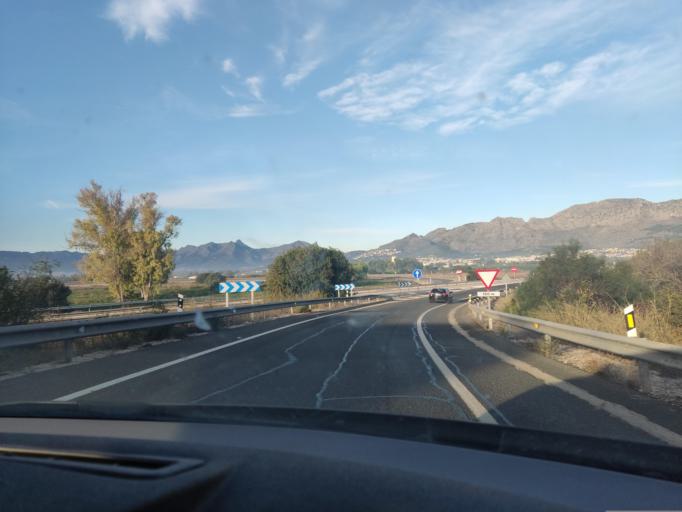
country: ES
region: Valencia
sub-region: Provincia de Alicante
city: Ondara
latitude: 38.8143
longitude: 0.0216
